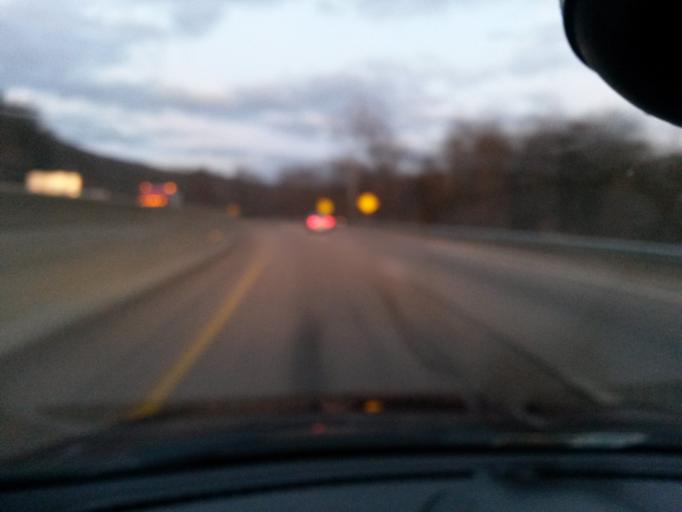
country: US
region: Virginia
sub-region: City of Covington
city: Fairlawn
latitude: 37.7759
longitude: -79.9378
